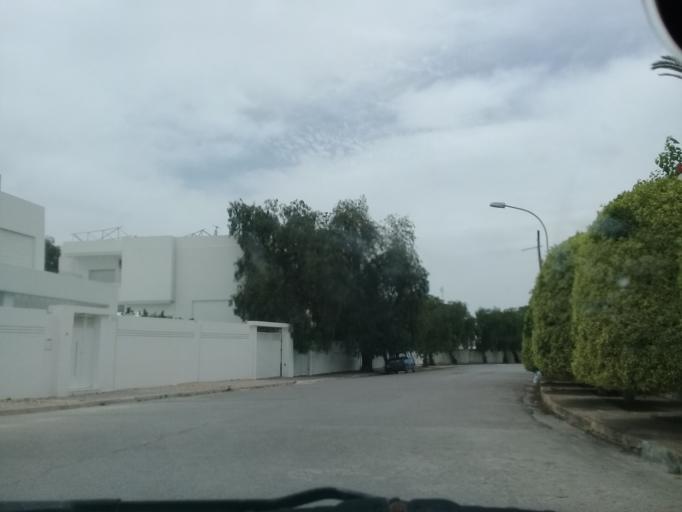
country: TN
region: Tunis
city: Tunis
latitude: 36.8413
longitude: 10.1641
